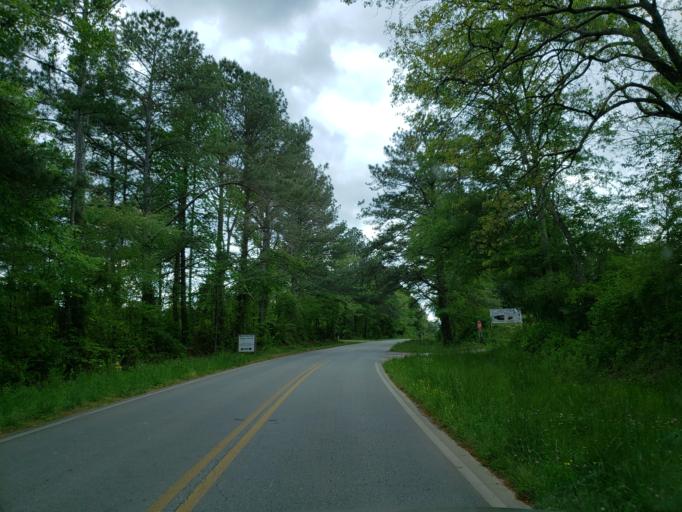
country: US
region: Georgia
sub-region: Haralson County
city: Tallapoosa
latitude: 33.7662
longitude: -85.3279
